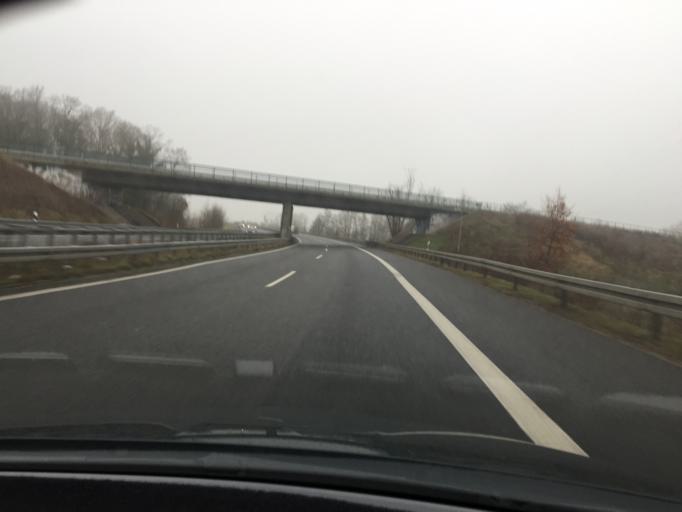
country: DE
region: Brandenburg
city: Rangsdorf
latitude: 52.3233
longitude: 13.4507
